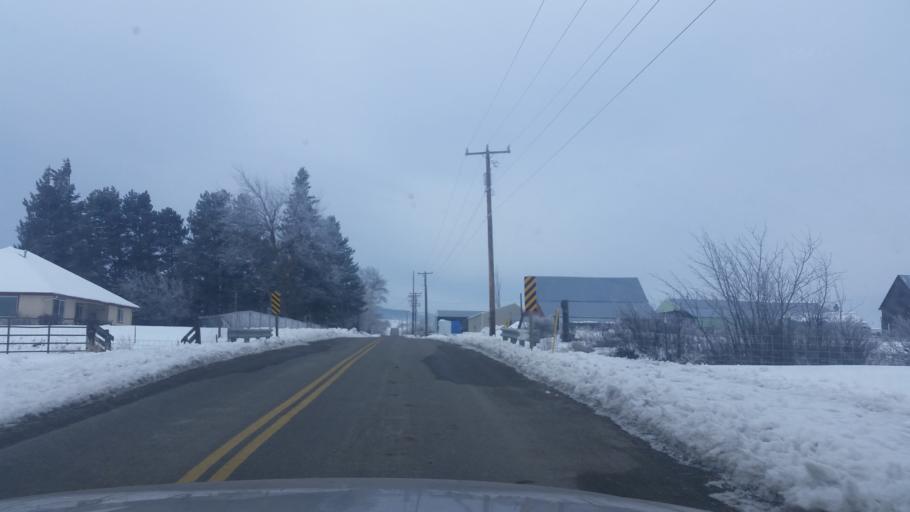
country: US
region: Washington
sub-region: Kittitas County
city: Ellensburg
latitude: 47.0800
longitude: -120.6904
